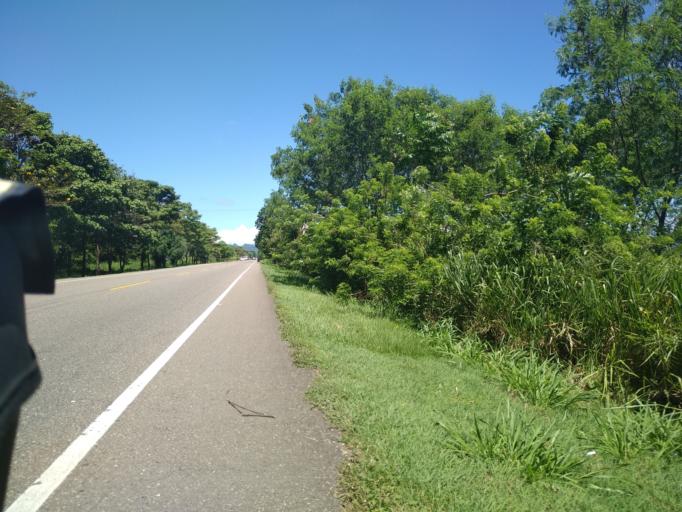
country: CO
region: Caldas
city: La Dorada
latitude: 5.3897
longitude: -74.7053
